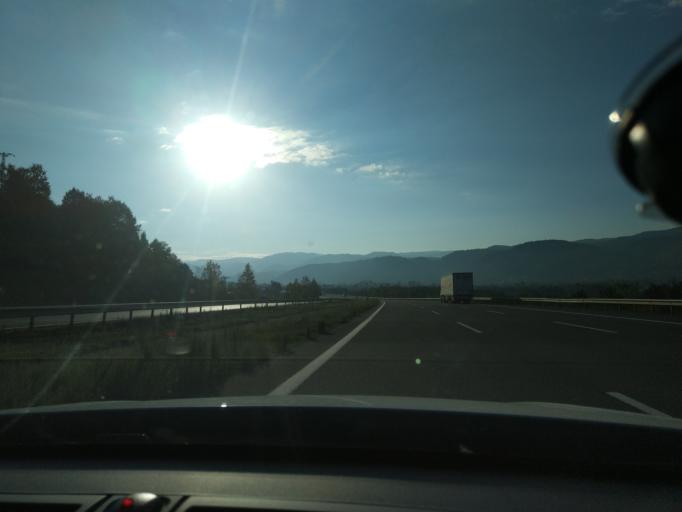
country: TR
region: Duzce
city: Kaynasli
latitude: 40.7879
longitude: 31.2936
